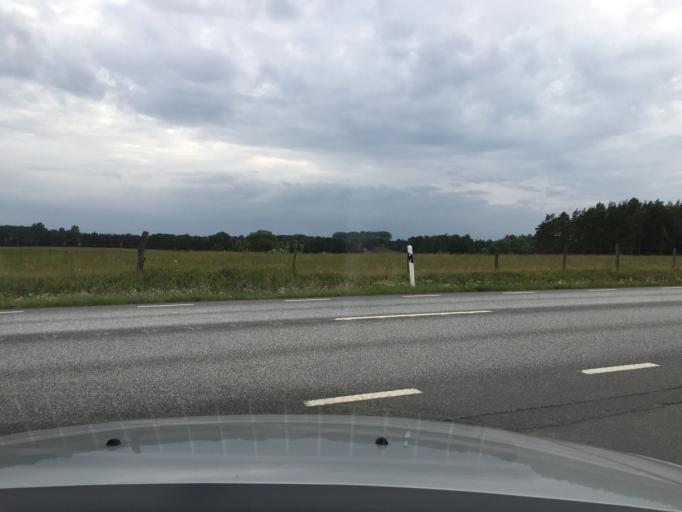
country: SE
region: Skane
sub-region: Kristianstads Kommun
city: Norra Asum
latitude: 55.9401
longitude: 14.0713
